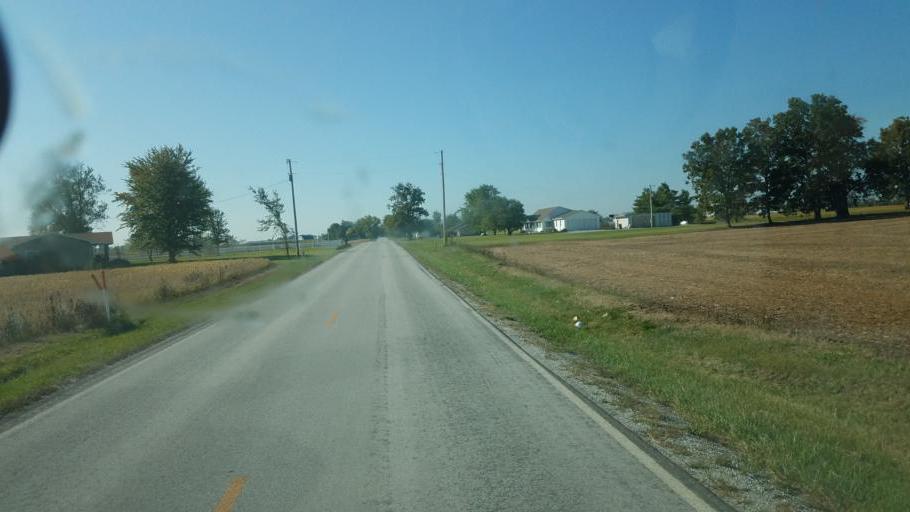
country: US
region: Ohio
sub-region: Hardin County
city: Kenton
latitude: 40.6186
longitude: -83.5809
